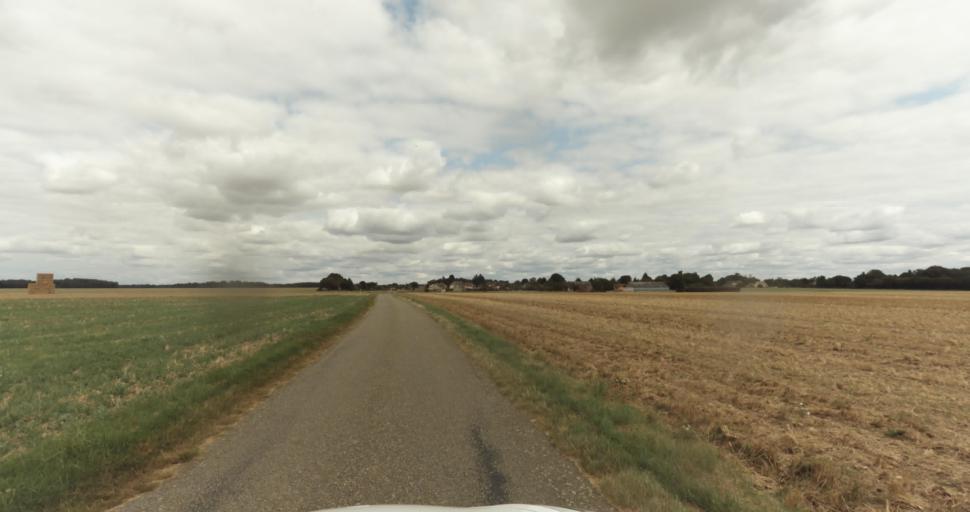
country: FR
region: Haute-Normandie
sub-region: Departement de l'Eure
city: Saint-Germain-sur-Avre
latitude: 48.7988
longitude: 1.2584
